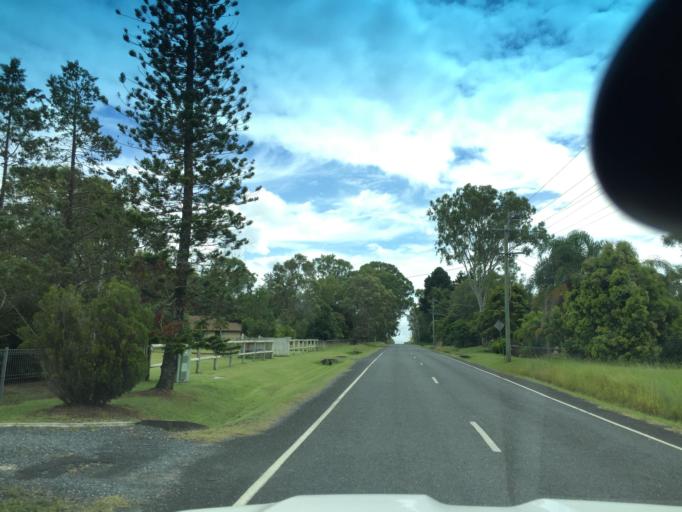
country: AU
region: Queensland
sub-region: Moreton Bay
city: Burpengary
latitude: -27.1683
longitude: 152.9886
